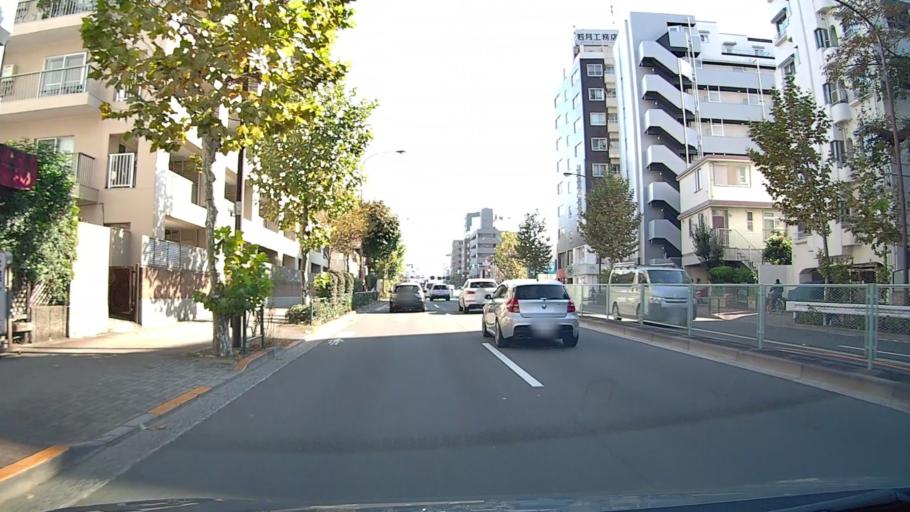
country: JP
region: Tokyo
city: Tokyo
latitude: 35.7332
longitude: 139.6690
